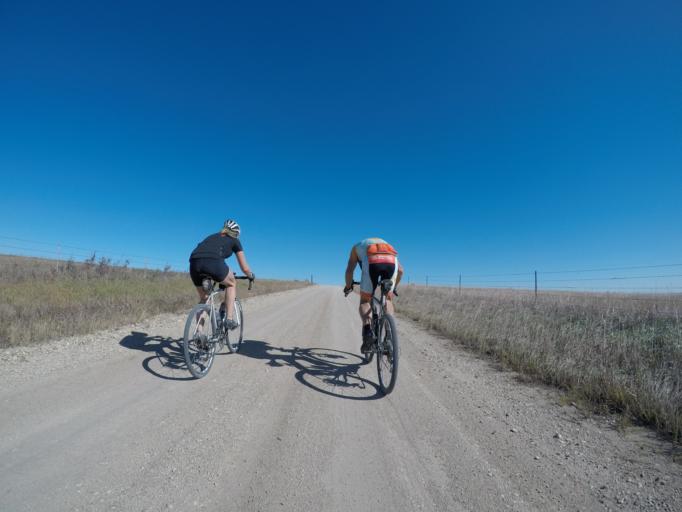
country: US
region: Kansas
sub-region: Wabaunsee County
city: Alma
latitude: 38.9567
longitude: -96.4698
